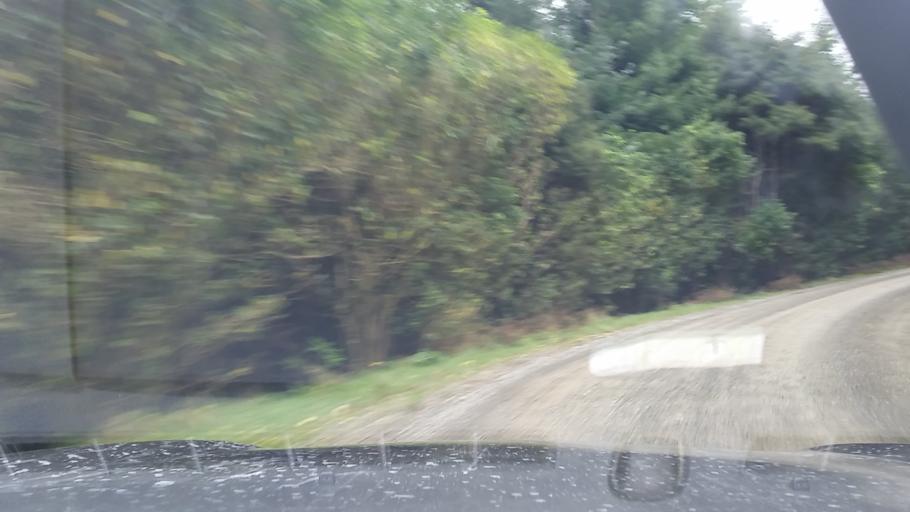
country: NZ
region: Marlborough
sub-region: Marlborough District
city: Picton
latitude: -41.1795
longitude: 173.9974
